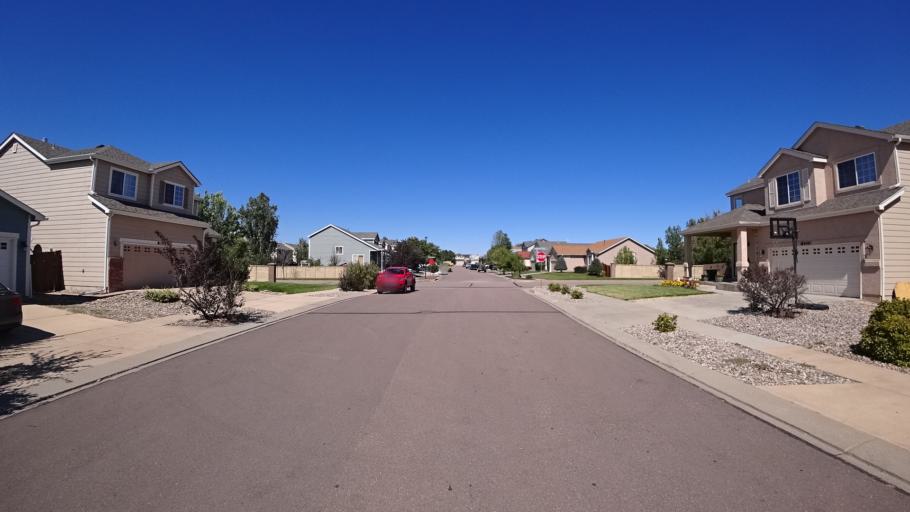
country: US
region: Colorado
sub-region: El Paso County
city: Security-Widefield
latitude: 38.7826
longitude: -104.7327
